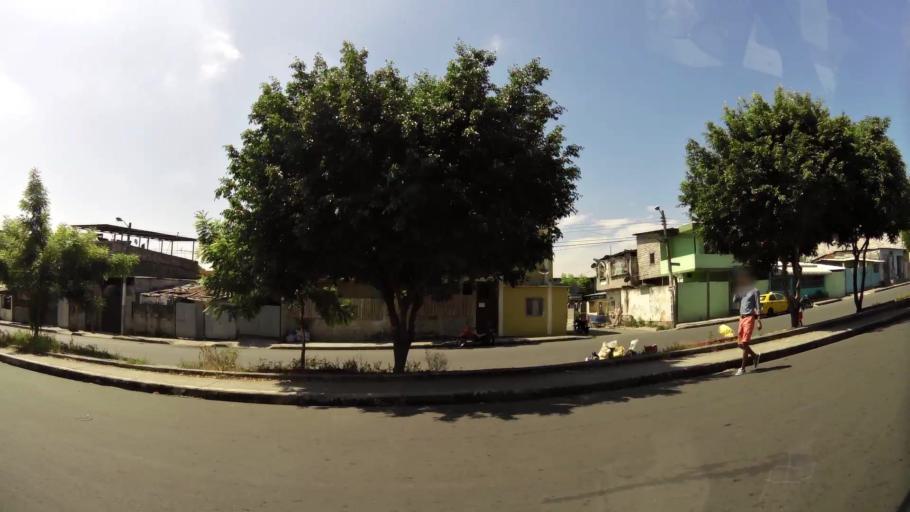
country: EC
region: Guayas
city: Guayaquil
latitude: -2.1277
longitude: -79.9231
